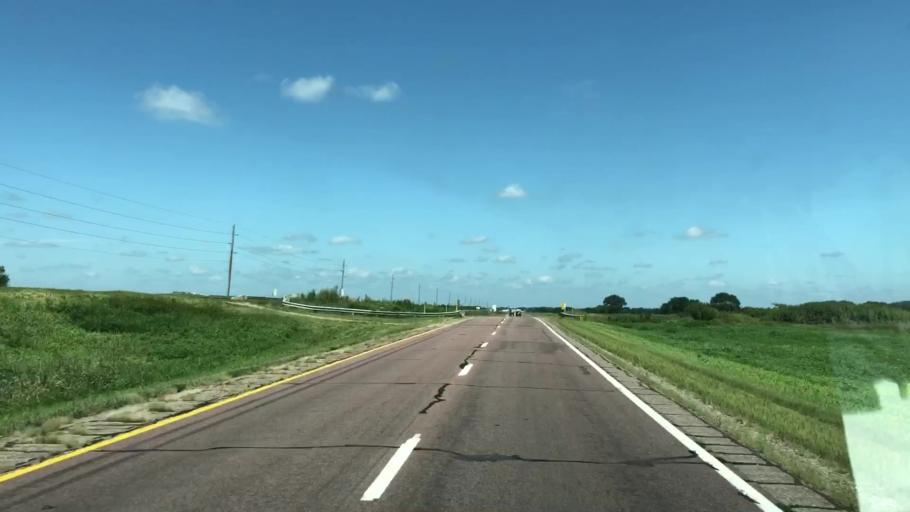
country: US
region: Iowa
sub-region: Plymouth County
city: Le Mars
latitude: 42.6837
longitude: -96.2667
